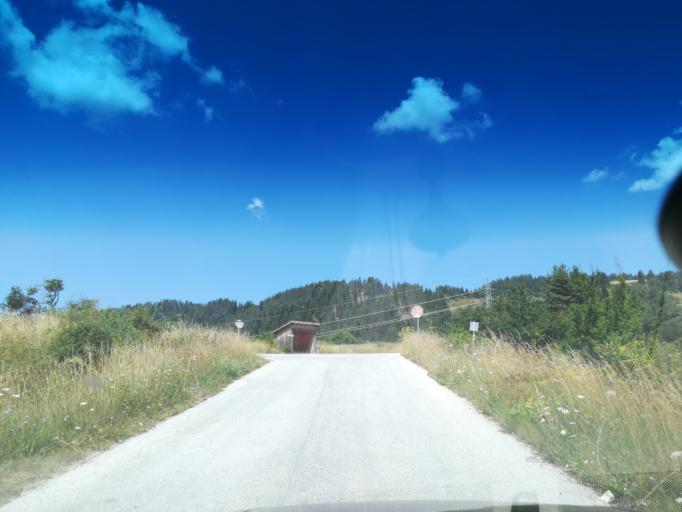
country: BG
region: Smolyan
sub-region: Obshtina Chepelare
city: Chepelare
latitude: 41.6700
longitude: 24.7779
